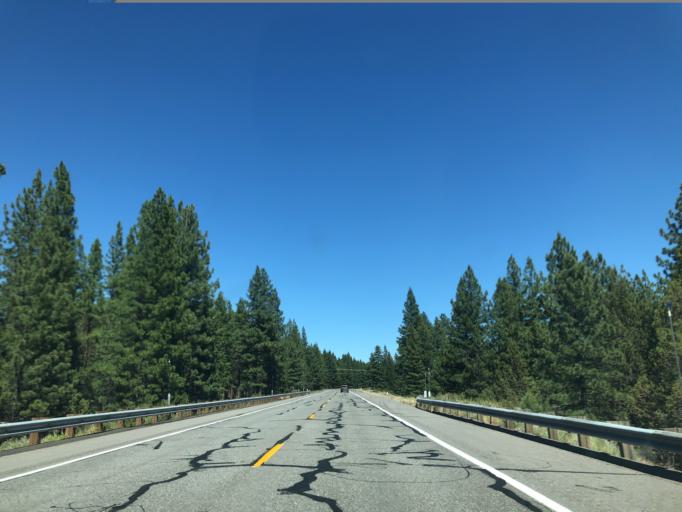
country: US
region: California
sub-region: Lassen County
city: Susanville
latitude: 40.4139
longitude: -120.7434
